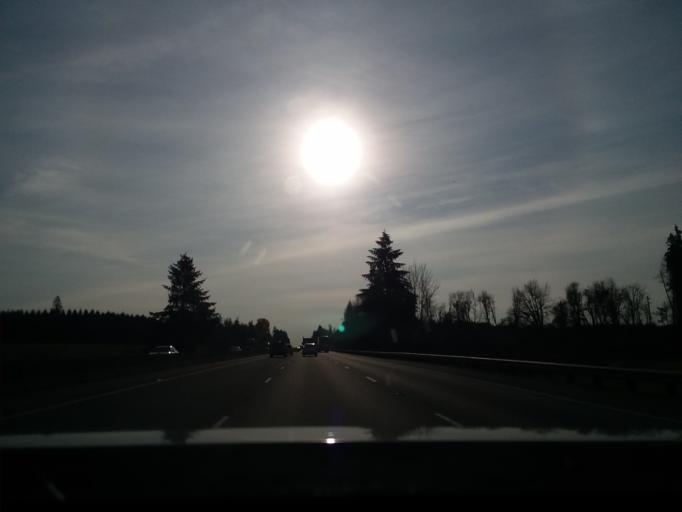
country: US
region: Washington
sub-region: Thurston County
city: Tumwater
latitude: 46.9132
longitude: -122.9517
